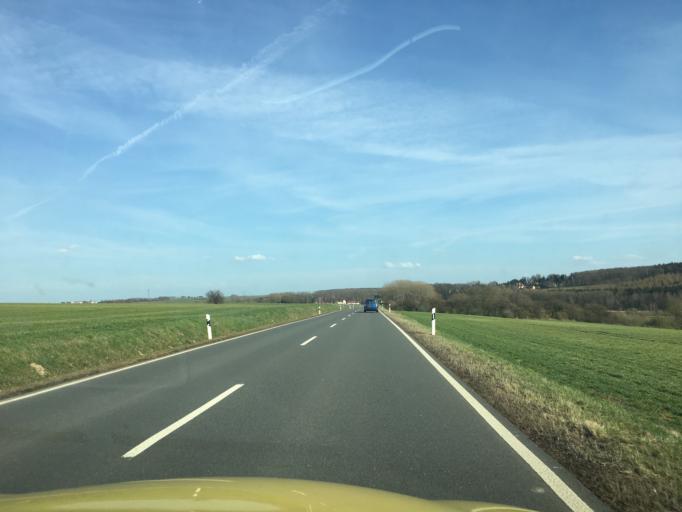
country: DE
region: Thuringia
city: Rastenberg
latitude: 51.2031
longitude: 11.4342
